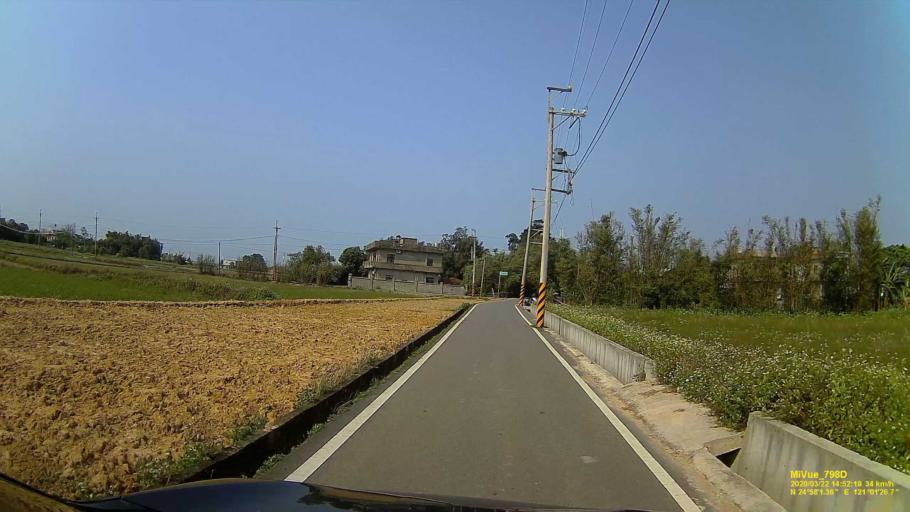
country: TW
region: Taiwan
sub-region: Hsinchu
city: Zhubei
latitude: 24.9672
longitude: 121.0241
